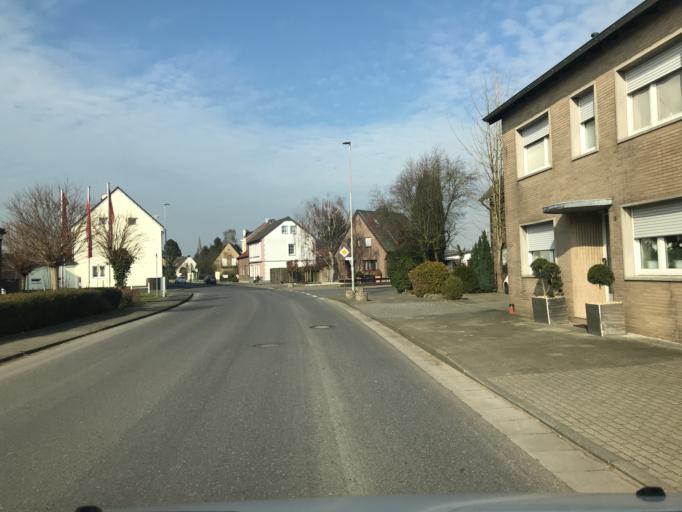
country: DE
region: North Rhine-Westphalia
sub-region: Regierungsbezirk Dusseldorf
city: Grefrath
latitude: 51.3191
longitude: 6.3860
